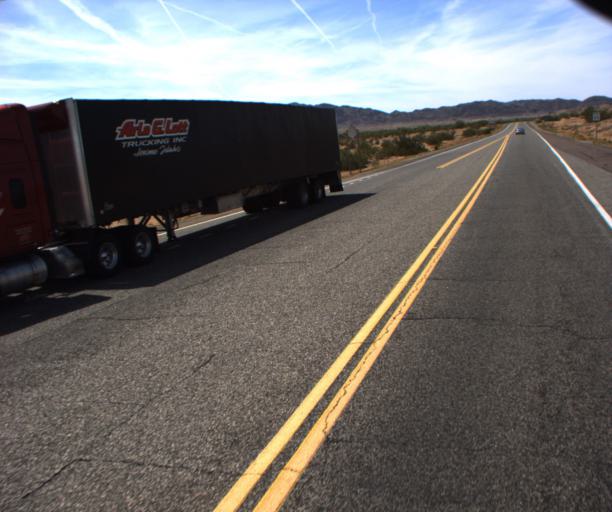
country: US
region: Arizona
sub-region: La Paz County
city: Parker
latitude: 33.9954
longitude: -114.2187
